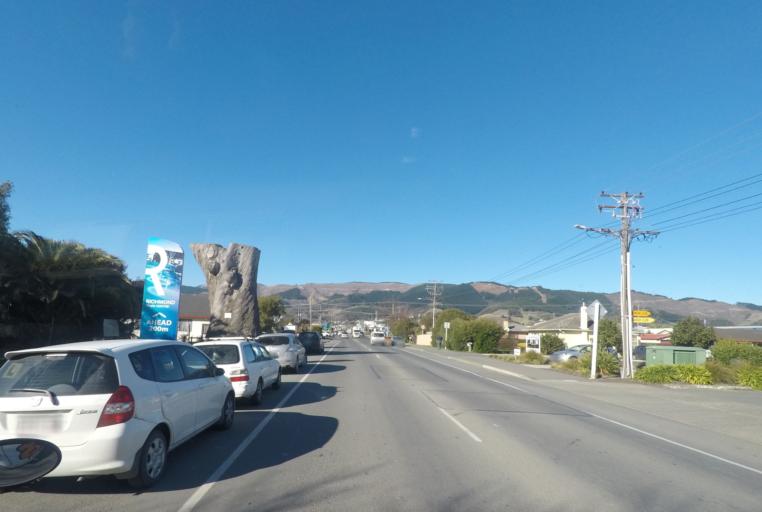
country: NZ
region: Tasman
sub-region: Tasman District
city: Richmond
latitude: -41.3348
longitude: 173.1800
